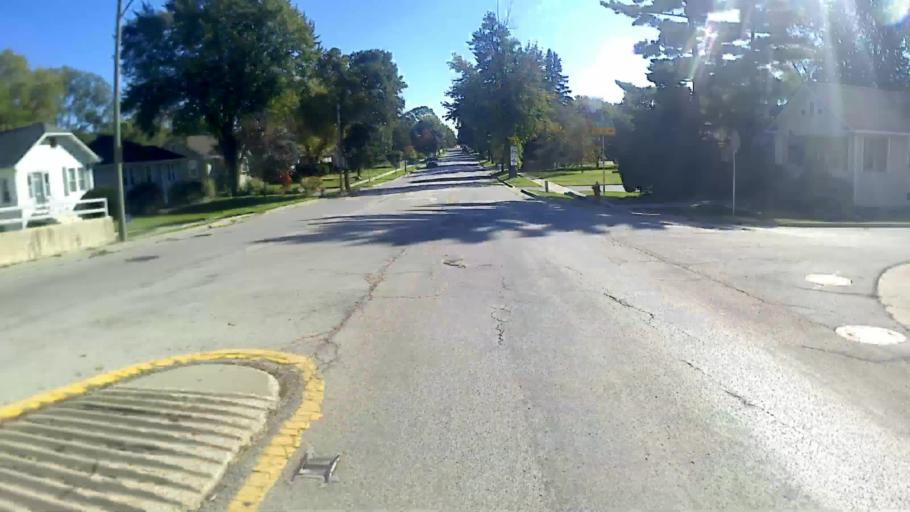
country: US
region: Illinois
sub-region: DuPage County
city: Villa Park
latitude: 41.8968
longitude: -87.9691
